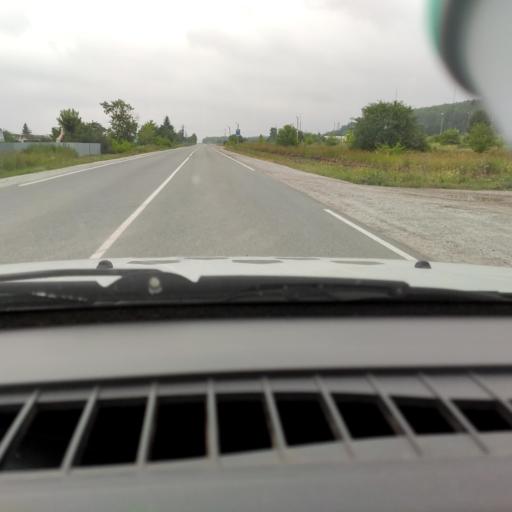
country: RU
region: Chelyabinsk
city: Miass
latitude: 54.9504
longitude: 60.0549
